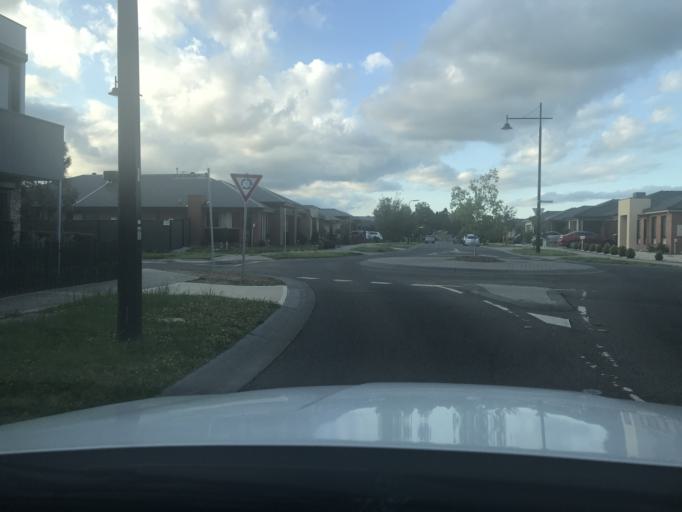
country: AU
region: Victoria
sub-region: Hume
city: Craigieburn
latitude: -37.5741
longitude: 144.9178
